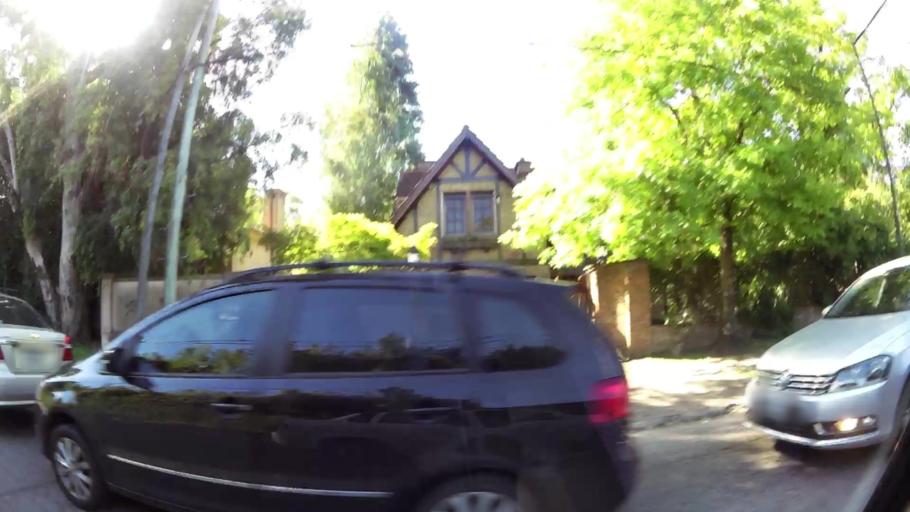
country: AR
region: Buenos Aires
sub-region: Partido de San Isidro
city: San Isidro
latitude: -34.4880
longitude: -58.5561
